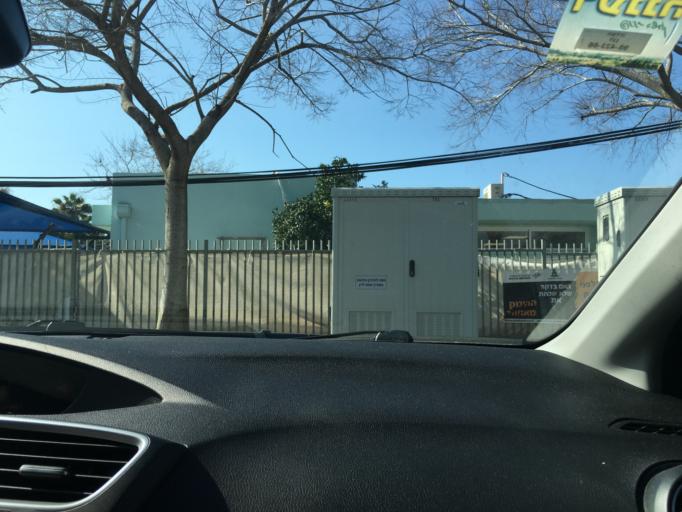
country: IL
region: Tel Aviv
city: Ramat HaSharon
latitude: 32.1492
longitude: 34.8309
